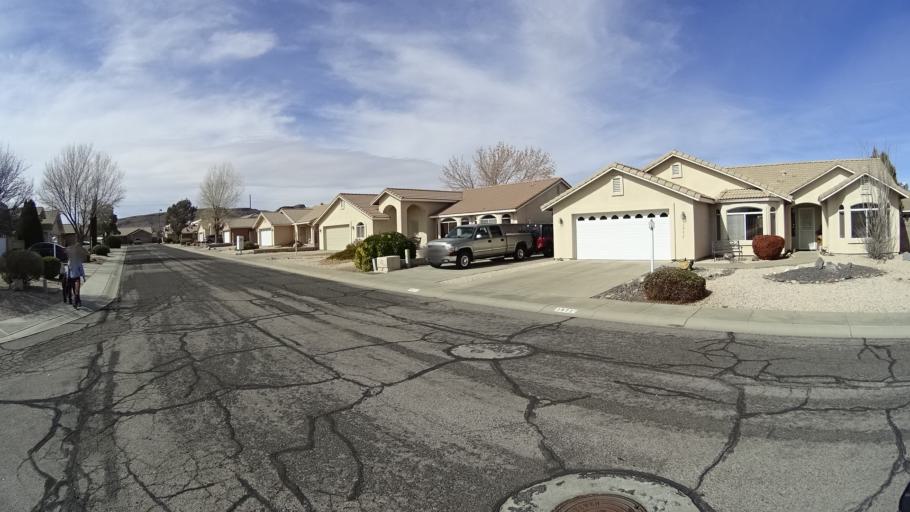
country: US
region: Arizona
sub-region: Mohave County
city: New Kingman-Butler
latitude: 35.2339
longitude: -114.0318
